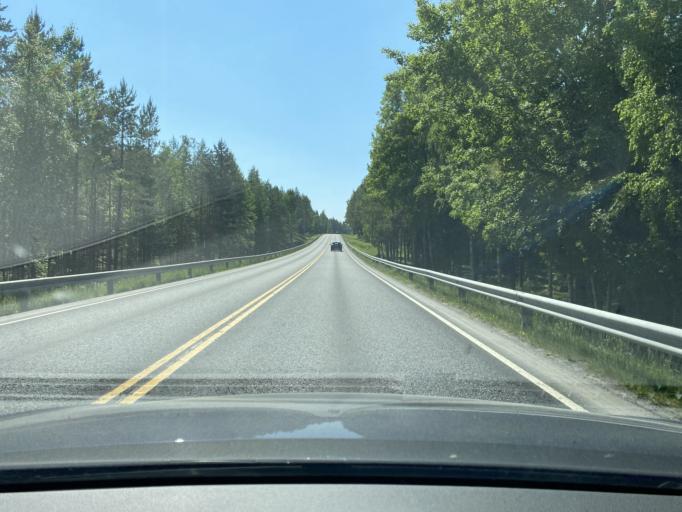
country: FI
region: Pirkanmaa
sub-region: Tampere
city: Nokia
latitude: 61.4114
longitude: 23.3048
